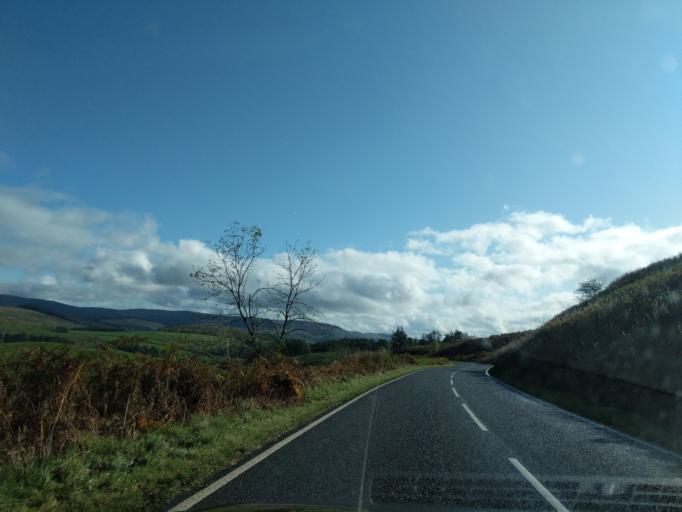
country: GB
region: Scotland
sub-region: Dumfries and Galloway
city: Moffat
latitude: 55.3604
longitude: -3.4756
